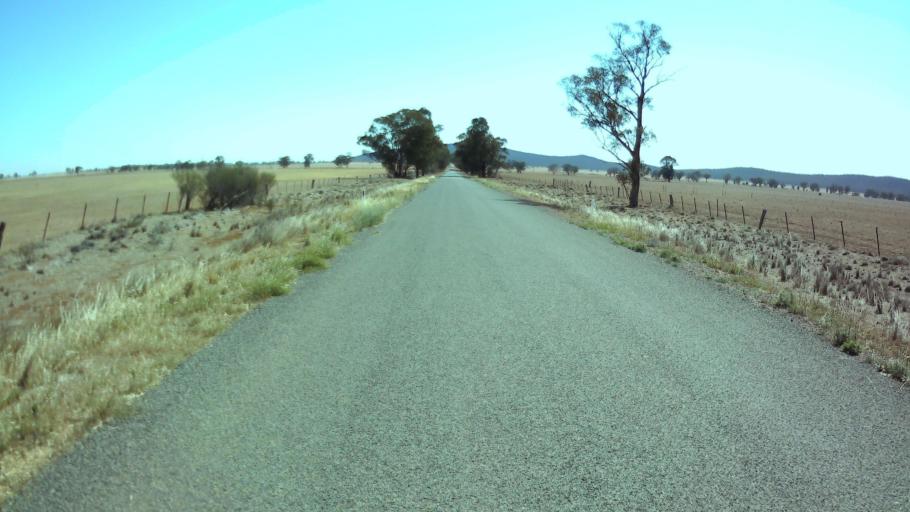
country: AU
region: New South Wales
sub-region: Weddin
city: Grenfell
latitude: -33.7108
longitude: 147.9116
